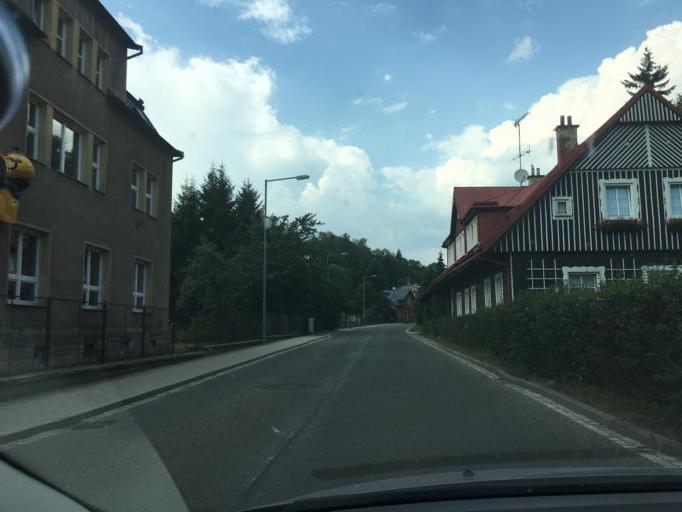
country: CZ
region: Kralovehradecky
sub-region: Okres Trutnov
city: Vrchlabi
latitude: 50.6347
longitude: 15.6074
